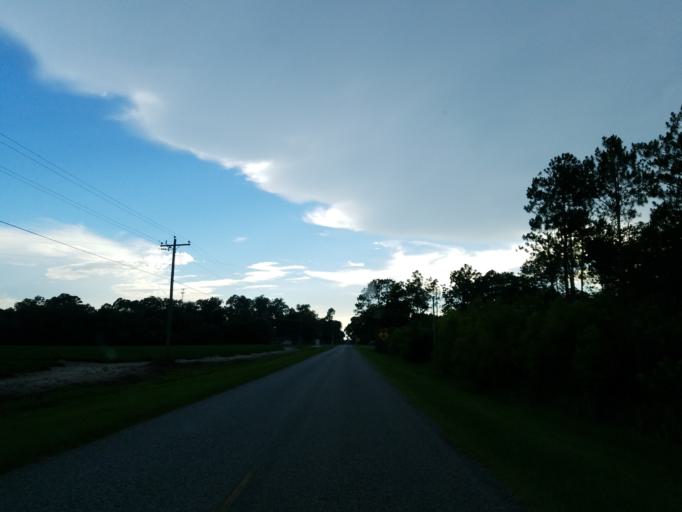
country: US
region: Georgia
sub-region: Cook County
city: Sparks
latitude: 31.2822
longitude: -83.4636
